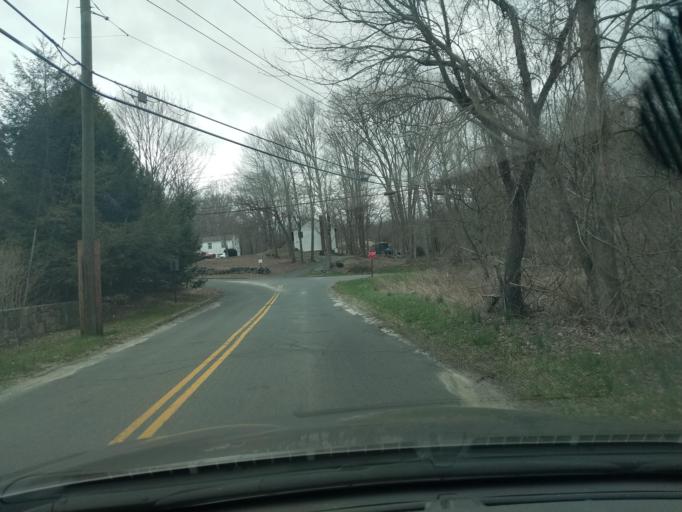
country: US
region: Connecticut
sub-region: Fairfield County
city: Newtown
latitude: 41.3603
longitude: -73.2832
